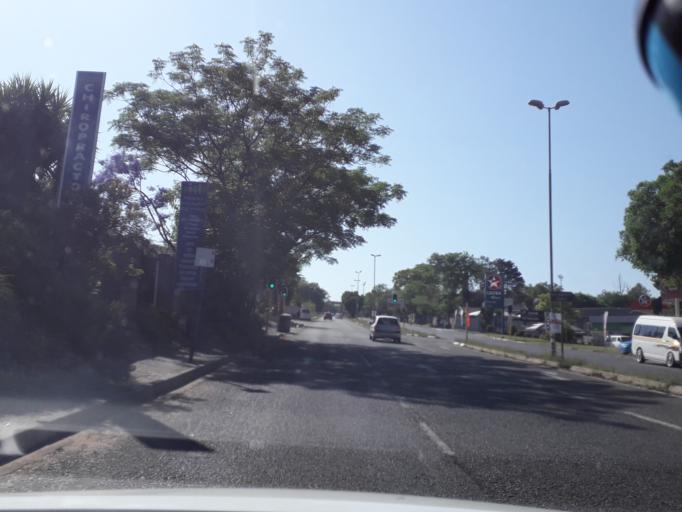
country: ZA
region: Gauteng
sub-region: City of Johannesburg Metropolitan Municipality
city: Roodepoort
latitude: -26.0917
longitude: 27.9770
